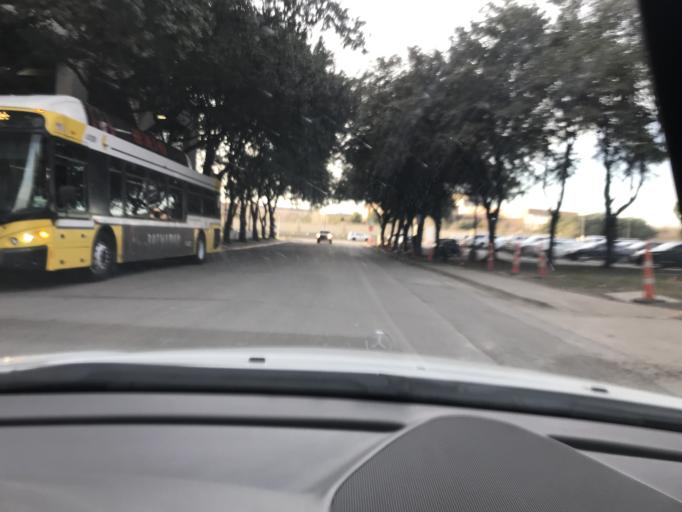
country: US
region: Texas
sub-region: Dallas County
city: Highland Park
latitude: 32.8391
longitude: -96.7753
